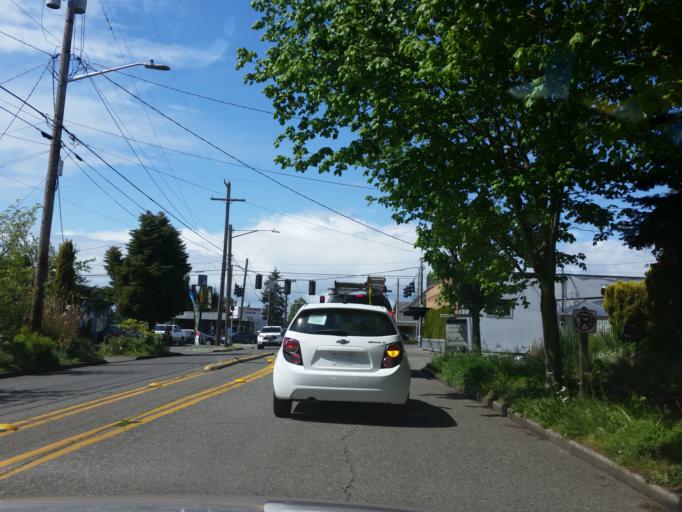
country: US
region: Washington
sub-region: King County
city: Shoreline
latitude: 47.6869
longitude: -122.3758
